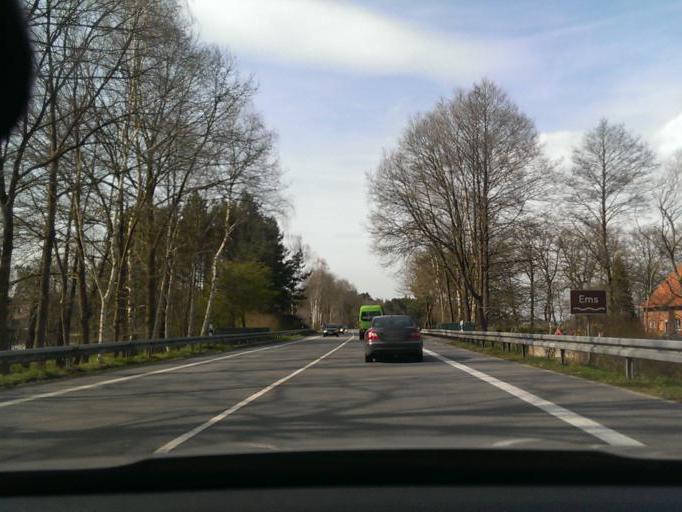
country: DE
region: North Rhine-Westphalia
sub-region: Regierungsbezirk Detmold
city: Hovelhof
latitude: 51.8478
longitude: 8.6654
